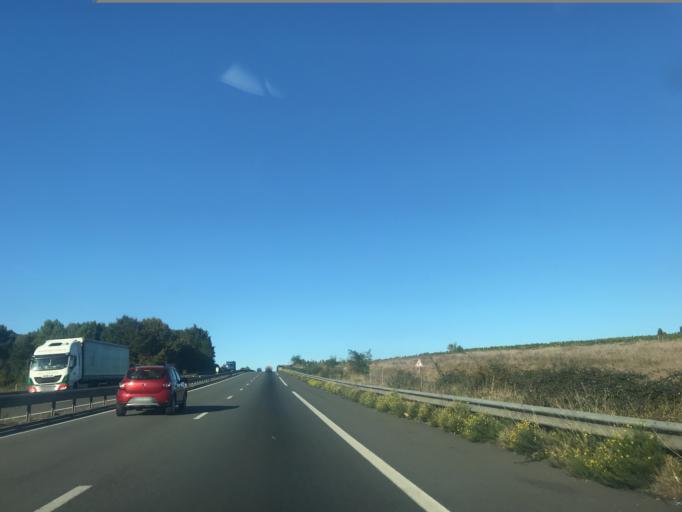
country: FR
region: Poitou-Charentes
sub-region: Departement de la Charente-Maritime
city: Montlieu-la-Garde
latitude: 45.2248
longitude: -0.2847
